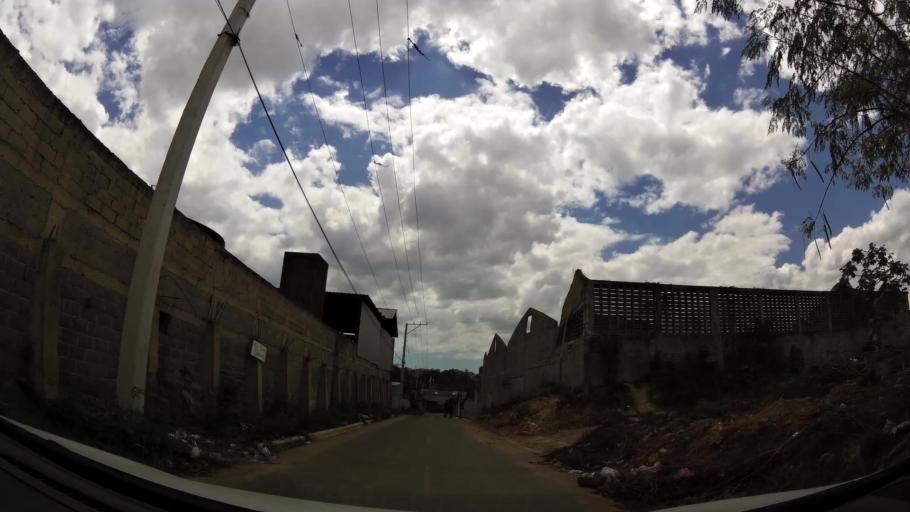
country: DO
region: Nacional
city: Ensanche Luperon
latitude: 18.5140
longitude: -69.9055
